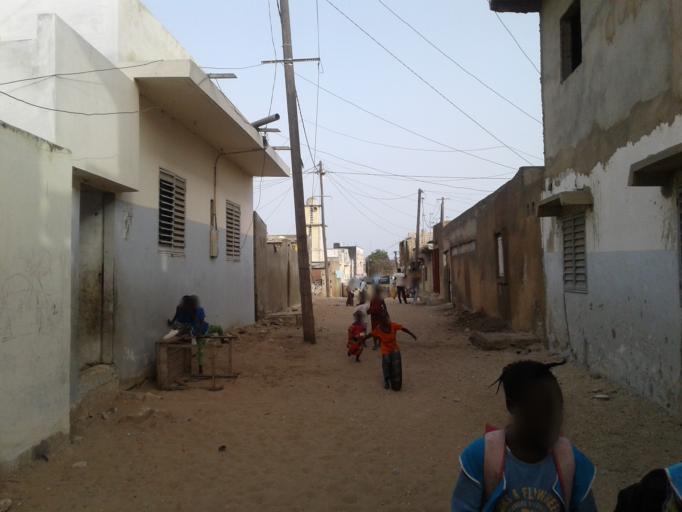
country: SN
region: Dakar
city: Pikine
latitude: 14.7652
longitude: -17.3798
